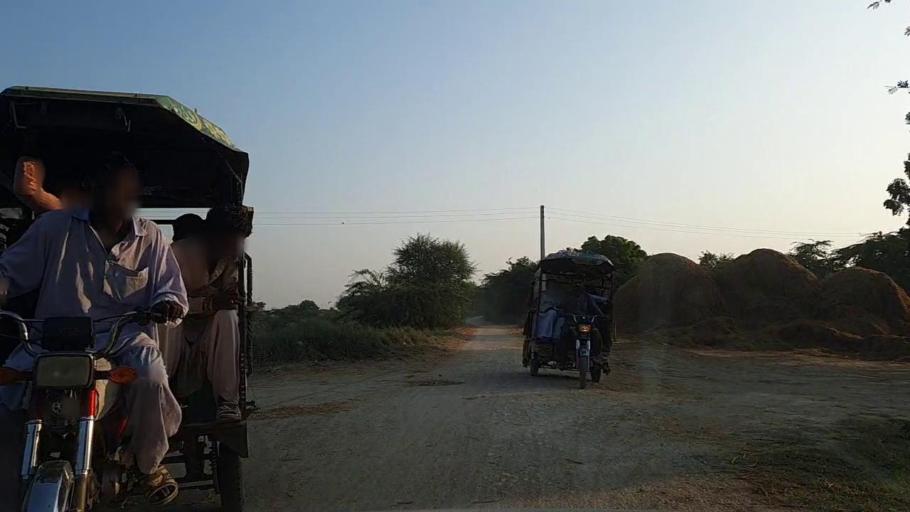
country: PK
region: Sindh
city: Daro Mehar
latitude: 24.7499
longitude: 68.1862
